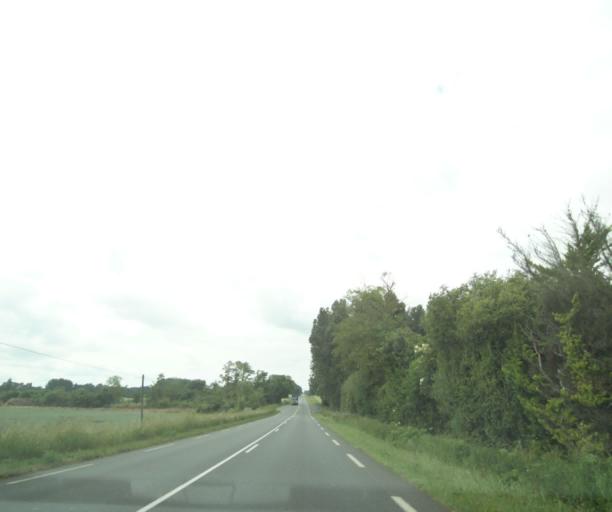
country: FR
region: Pays de la Loire
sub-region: Departement de Maine-et-Loire
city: Distre
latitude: 47.1923
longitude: -0.1273
